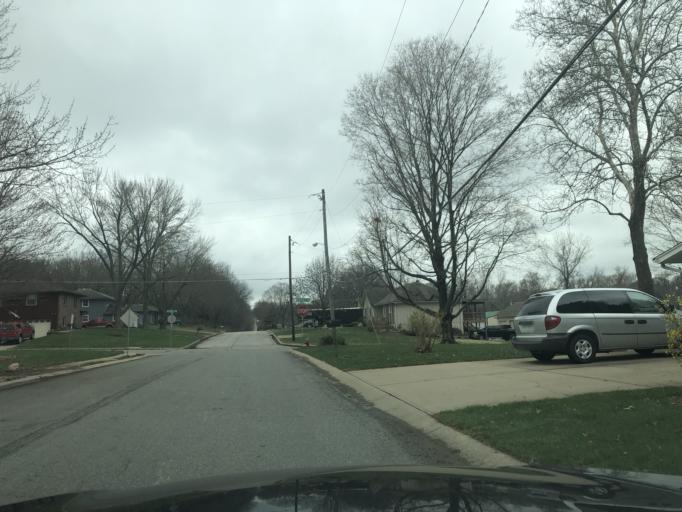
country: US
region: Kansas
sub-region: Leavenworth County
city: Leavenworth
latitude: 39.2818
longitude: -94.9138
